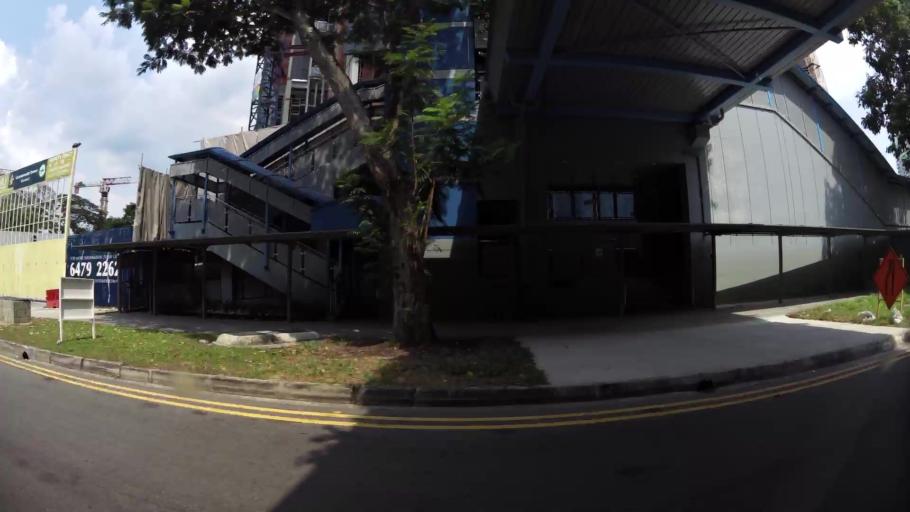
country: SG
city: Singapore
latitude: 1.2956
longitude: 103.8057
